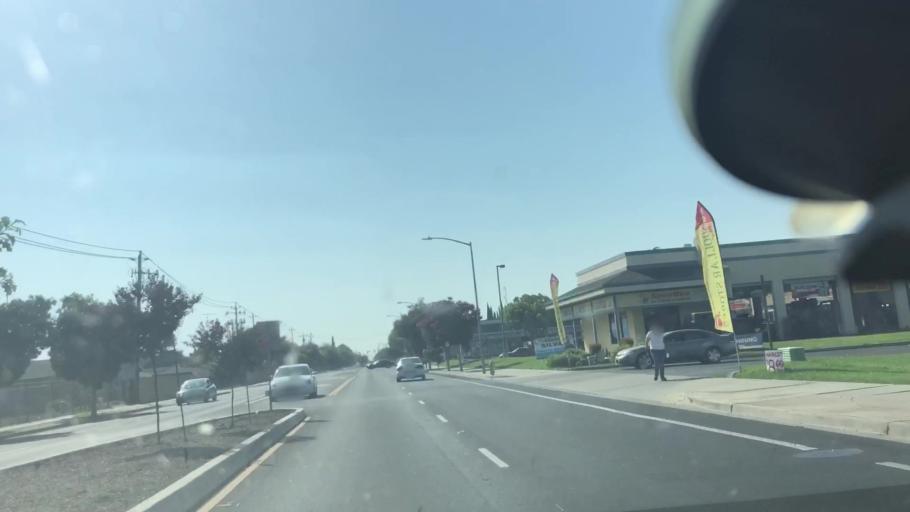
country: US
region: California
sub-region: San Joaquin County
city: Manteca
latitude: 37.8120
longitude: -121.2186
